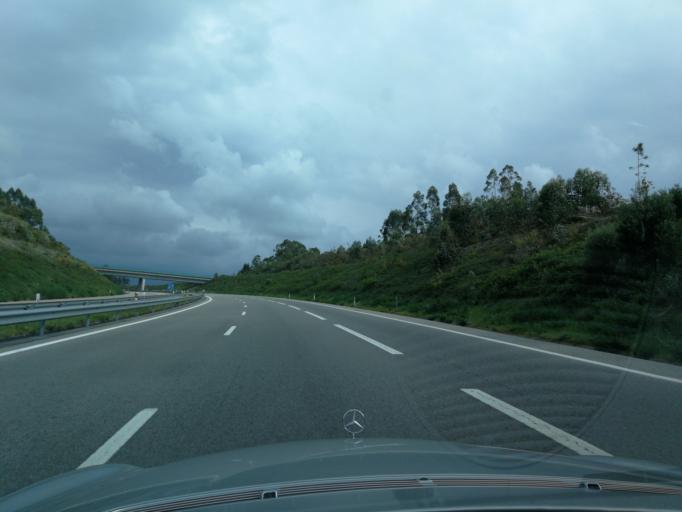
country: PT
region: Porto
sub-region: Vila do Conde
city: Arvore
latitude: 41.3801
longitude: -8.6609
